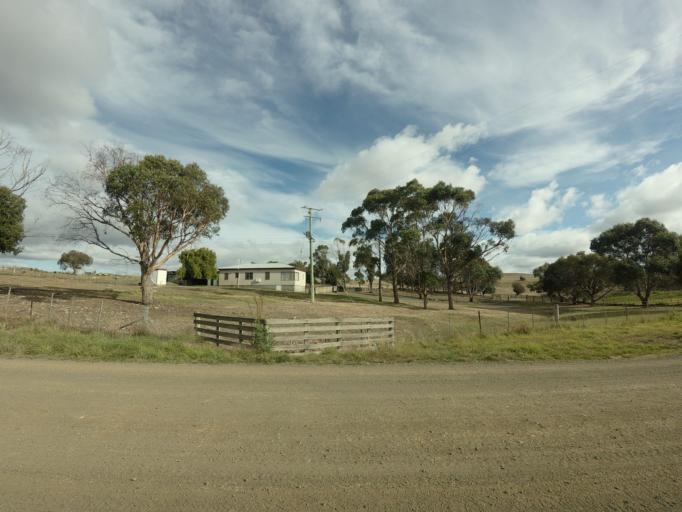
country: AU
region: Tasmania
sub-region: Brighton
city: Bridgewater
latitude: -42.4443
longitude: 147.2270
